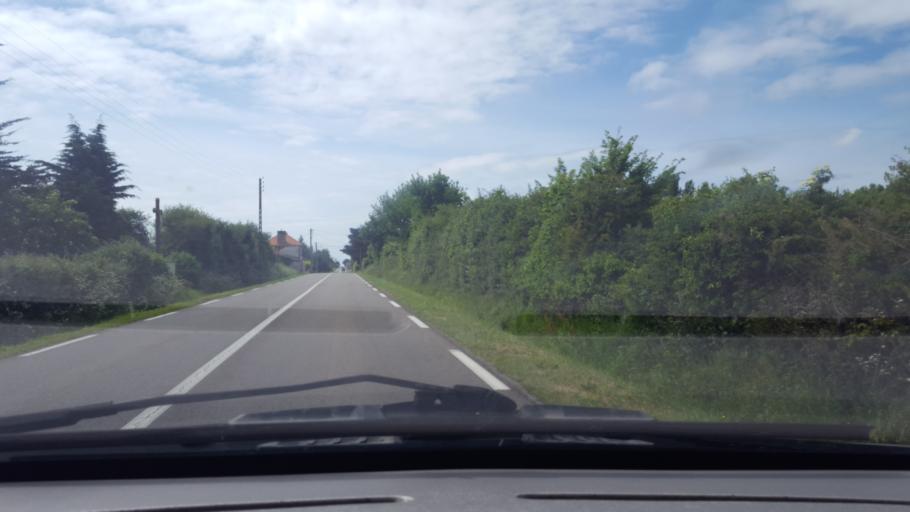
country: FR
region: Pays de la Loire
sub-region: Departement de la Loire-Atlantique
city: Bourgneuf-en-Retz
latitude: 47.0284
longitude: -1.8948
